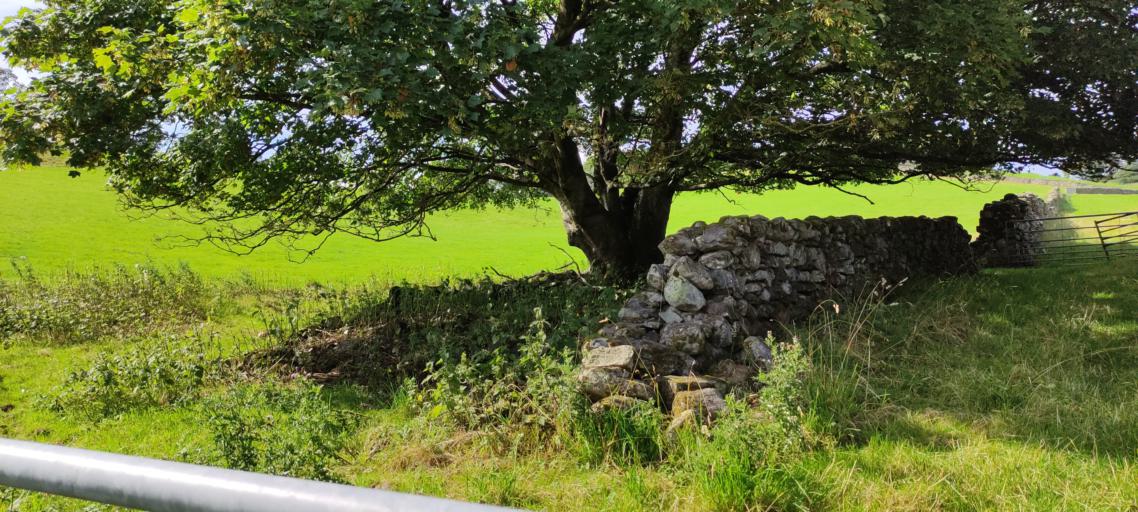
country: GB
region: England
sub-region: Cumbria
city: Penrith
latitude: 54.5531
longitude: -2.7566
